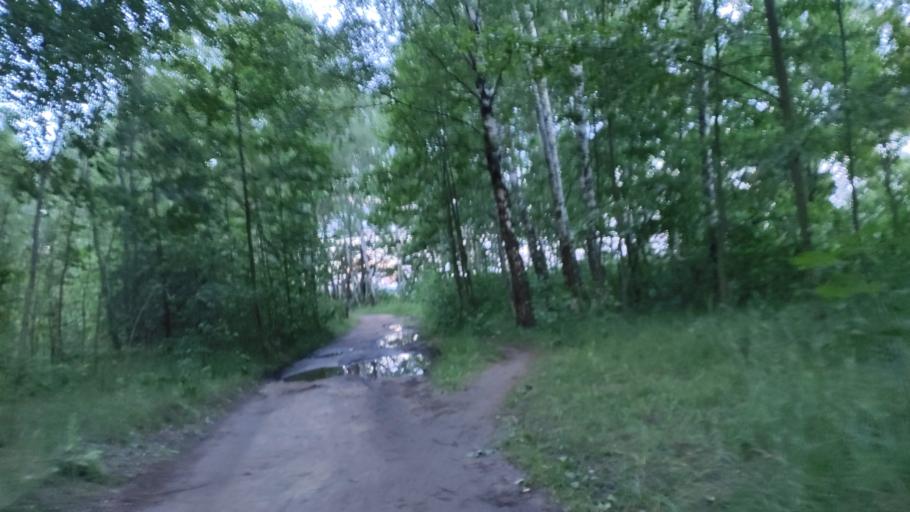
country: BY
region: Minsk
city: Zhdanovichy
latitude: 53.9501
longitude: 27.4699
